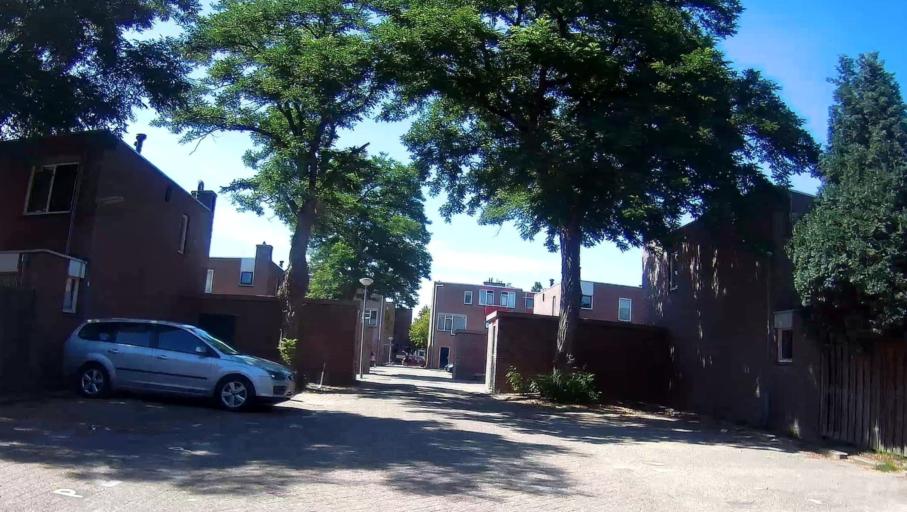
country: NL
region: South Holland
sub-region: Gemeente Capelle aan den IJssel
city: Capelle-West
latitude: 51.8948
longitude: 4.5703
